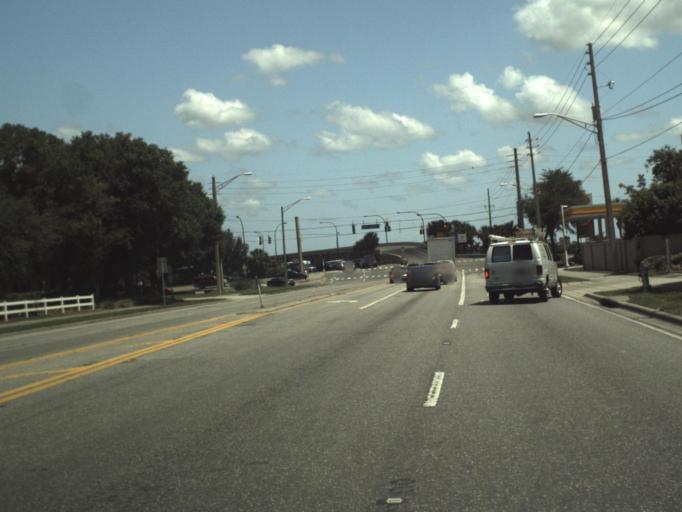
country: US
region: Florida
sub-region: Orange County
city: Azalea Park
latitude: 28.5362
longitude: -81.3311
